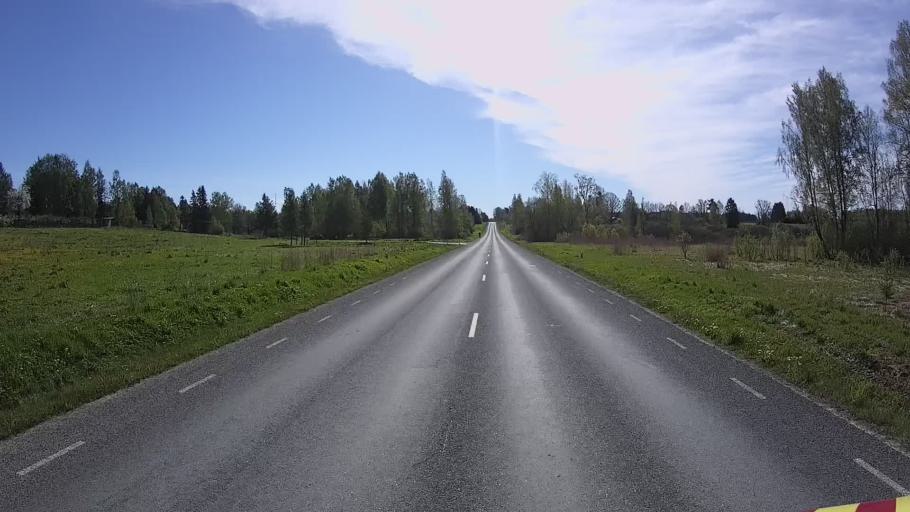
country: EE
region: Polvamaa
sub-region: Polva linn
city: Polva
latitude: 58.1578
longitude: 27.1714
